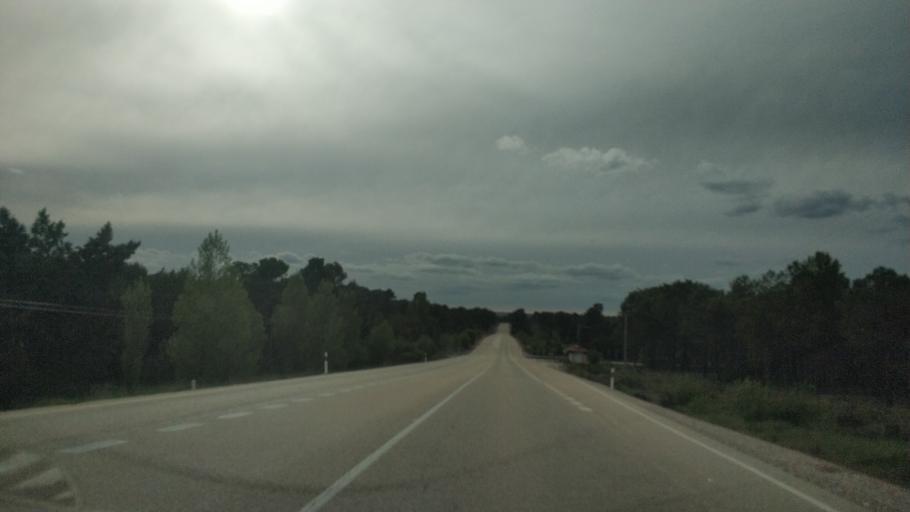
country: ES
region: Castille and Leon
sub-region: Provincia de Soria
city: Valdenebro
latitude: 41.5594
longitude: -2.9717
